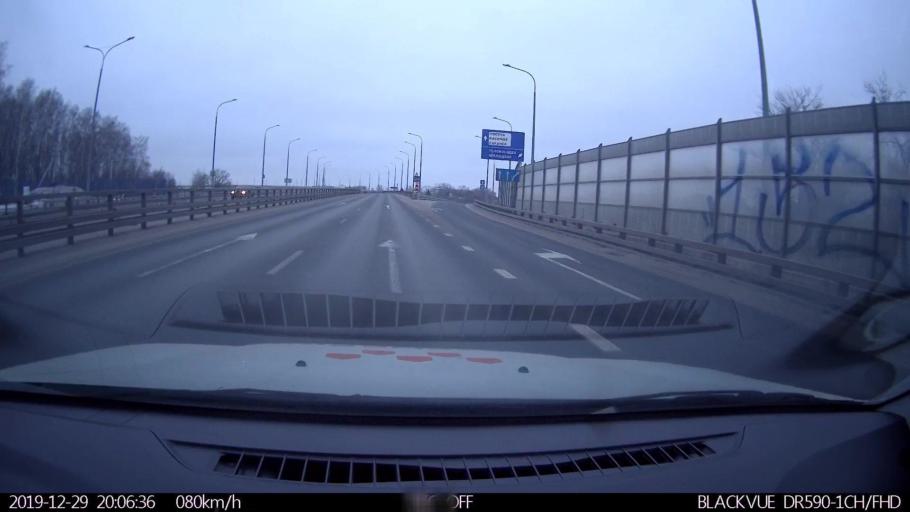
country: RU
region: Nizjnij Novgorod
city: Neklyudovo
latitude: 56.3963
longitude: 44.0002
